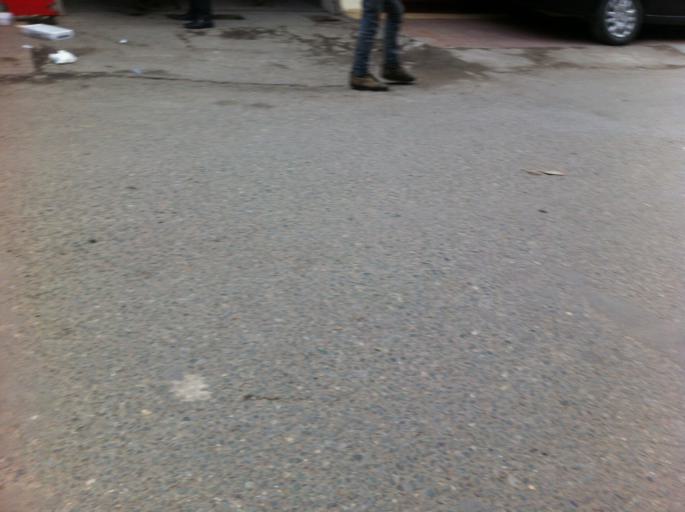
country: IN
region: Punjab
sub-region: Kapurthala
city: Phagwara
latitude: 31.2227
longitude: 75.7700
